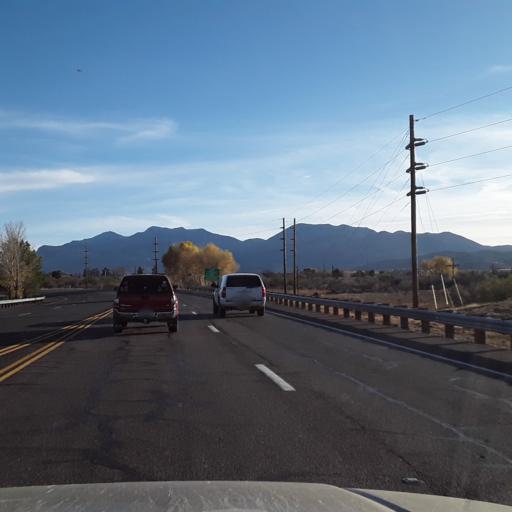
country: US
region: Arizona
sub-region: Cochise County
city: Sierra Vista
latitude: 31.5592
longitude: -110.3086
